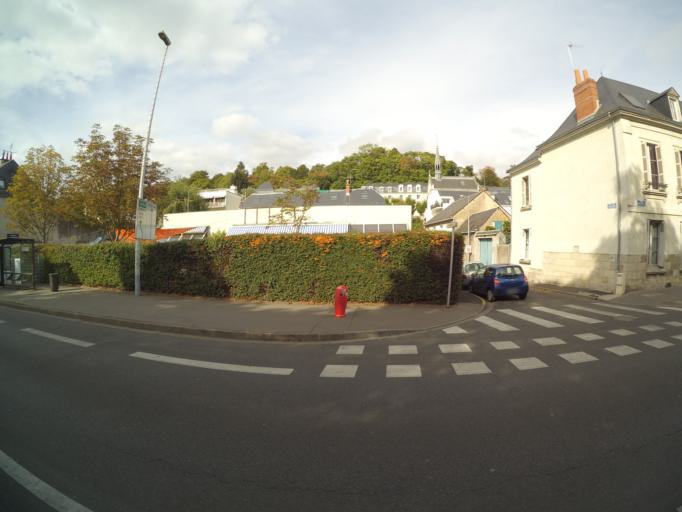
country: FR
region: Centre
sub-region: Departement d'Indre-et-Loire
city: Tours
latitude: 47.4017
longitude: 0.6891
